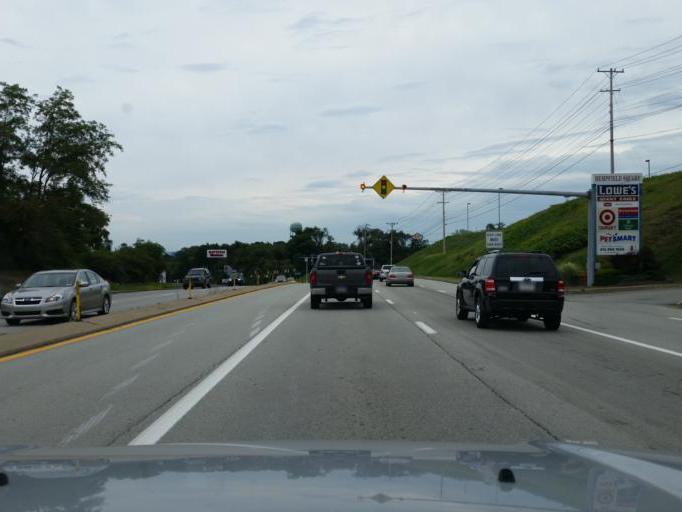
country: US
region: Pennsylvania
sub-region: Westmoreland County
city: Jeannette
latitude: 40.3066
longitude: -79.5944
